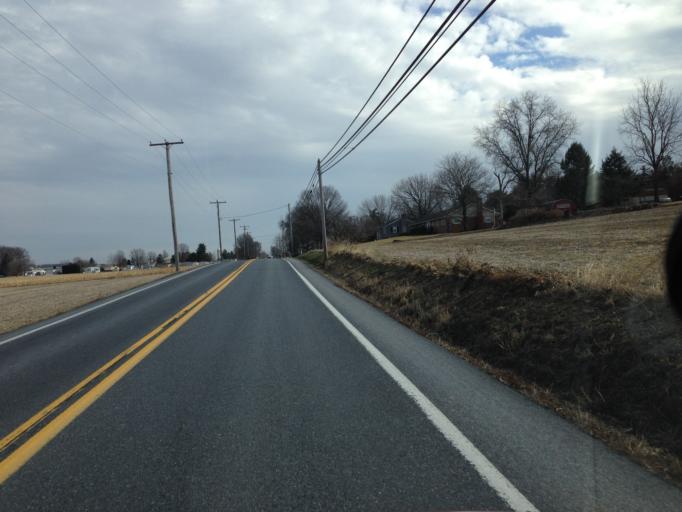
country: US
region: Pennsylvania
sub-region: Lancaster County
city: Penryn
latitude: 40.1793
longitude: -76.3561
